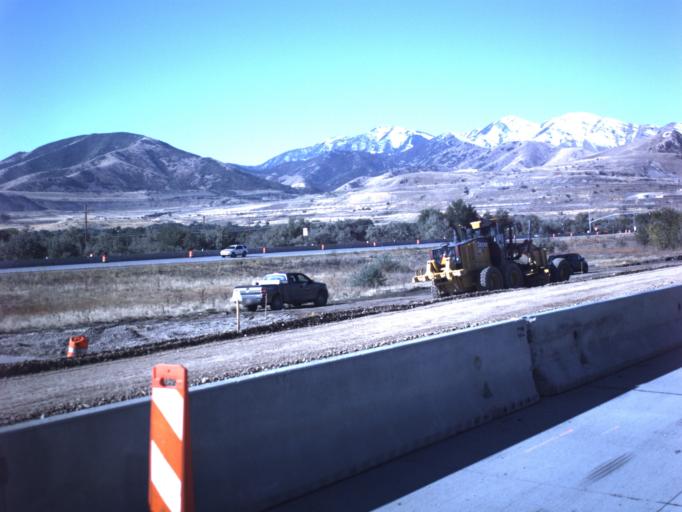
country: US
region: Utah
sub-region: Salt Lake County
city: Magna
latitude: 40.7182
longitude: -112.0880
